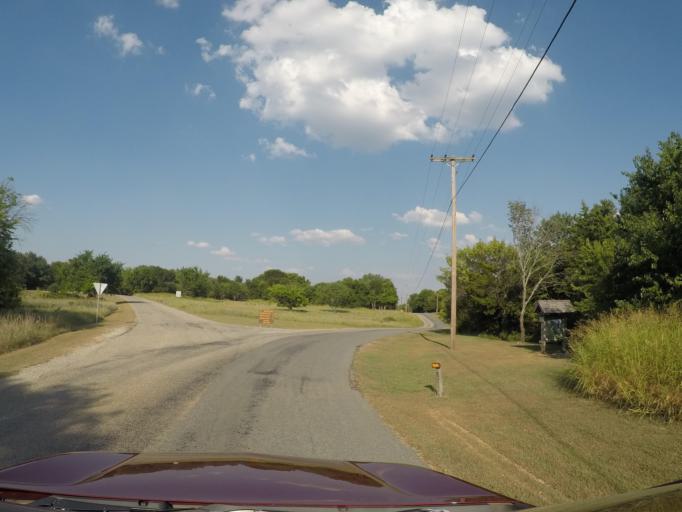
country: US
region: Texas
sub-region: Grayson County
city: Preston
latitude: 33.8221
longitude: -96.6132
